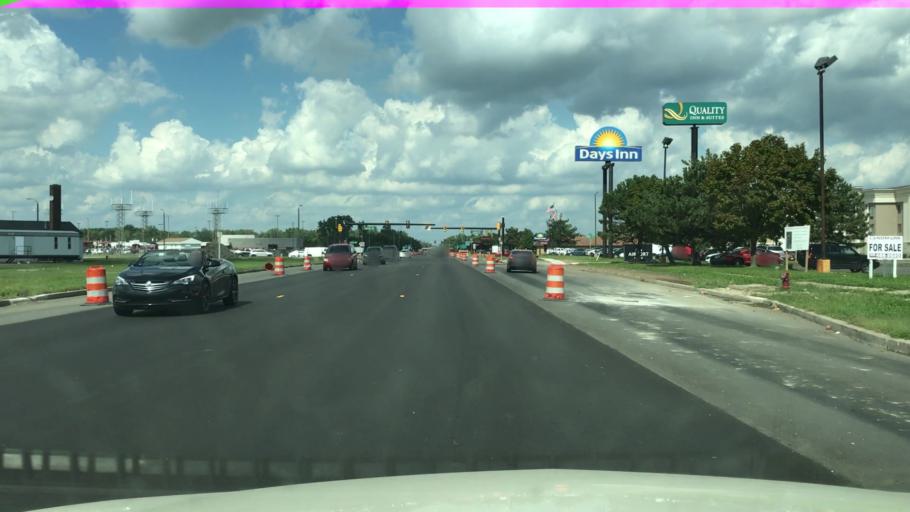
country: US
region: Michigan
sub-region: Wayne County
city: Taylor
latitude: 42.2344
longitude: -83.3276
